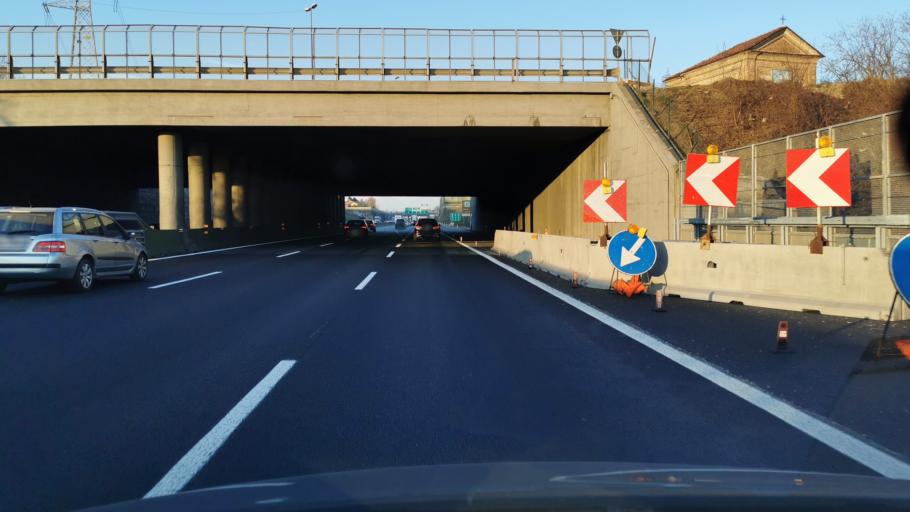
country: IT
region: Piedmont
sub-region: Provincia di Torino
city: Venaria Reale
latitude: 45.1249
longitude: 7.6536
